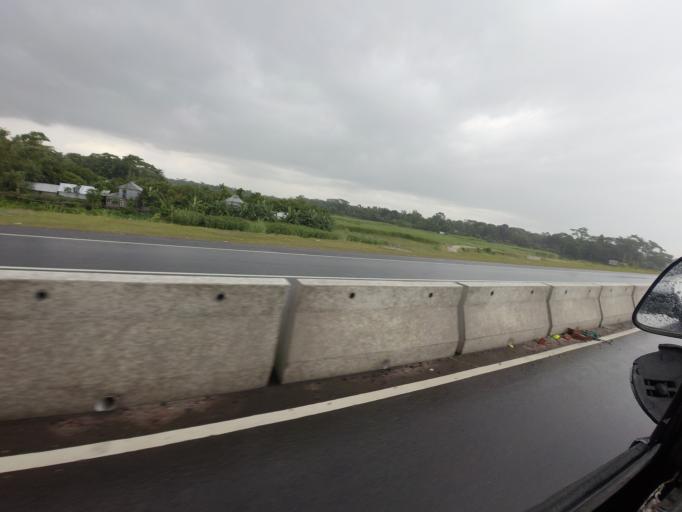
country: BD
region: Dhaka
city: Char Bhadrasan
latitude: 23.3997
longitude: 90.1987
